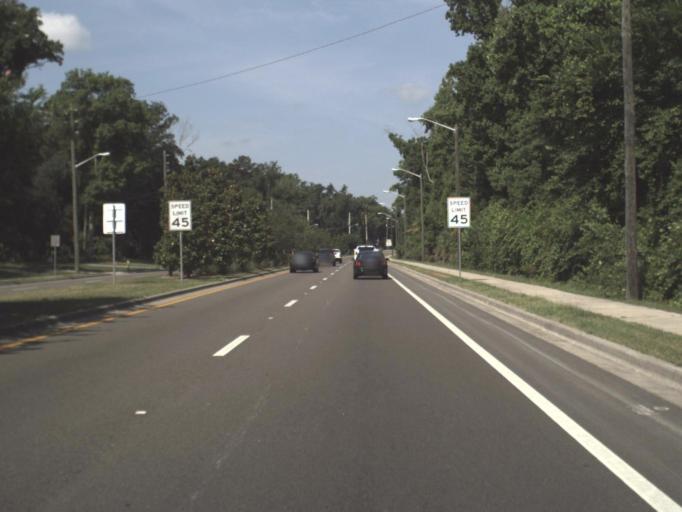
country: US
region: Florida
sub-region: Duval County
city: Atlantic Beach
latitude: 30.3546
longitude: -81.5251
